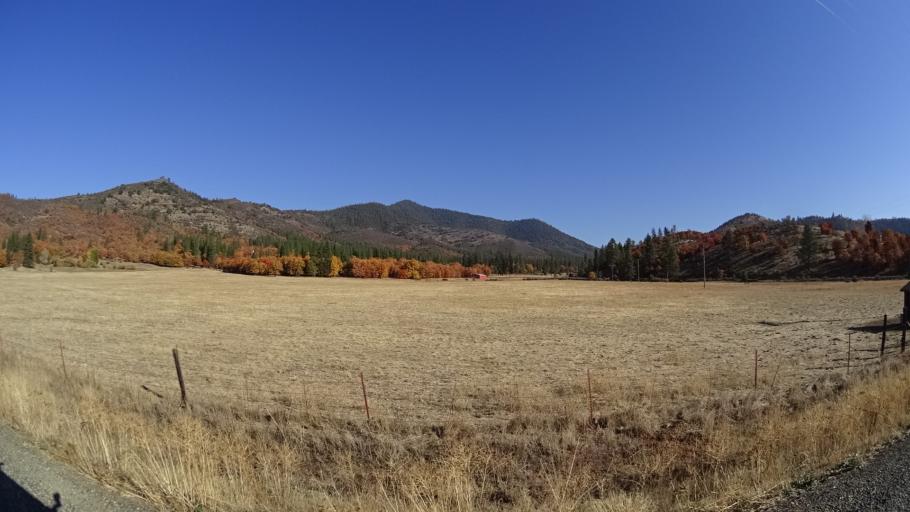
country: US
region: California
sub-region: Siskiyou County
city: Yreka
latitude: 41.6418
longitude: -122.9222
